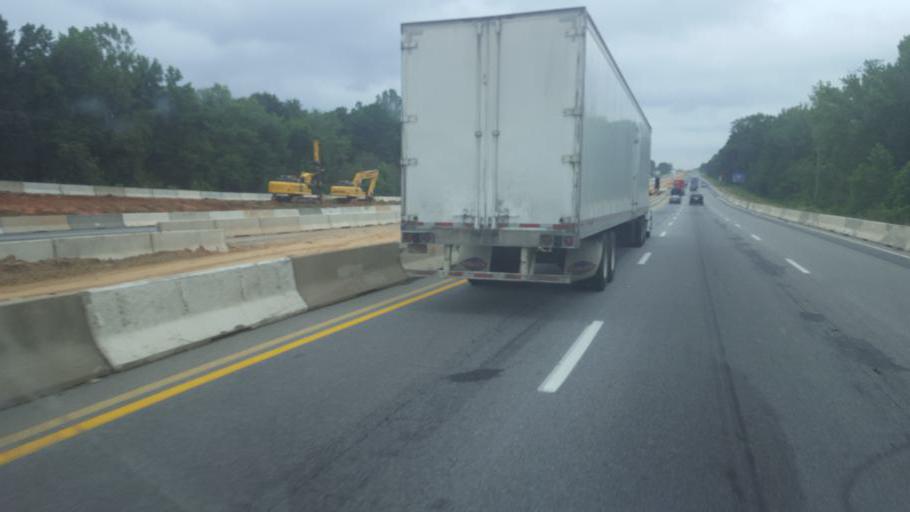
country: US
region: North Carolina
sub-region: Gaston County
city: Davidson
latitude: 35.5375
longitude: -80.8607
